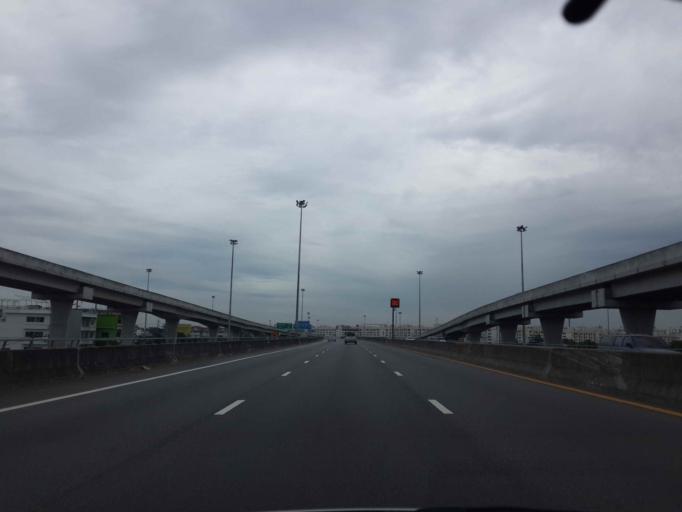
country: TH
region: Bangkok
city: Bang Khen
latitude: 13.8492
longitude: 100.6392
